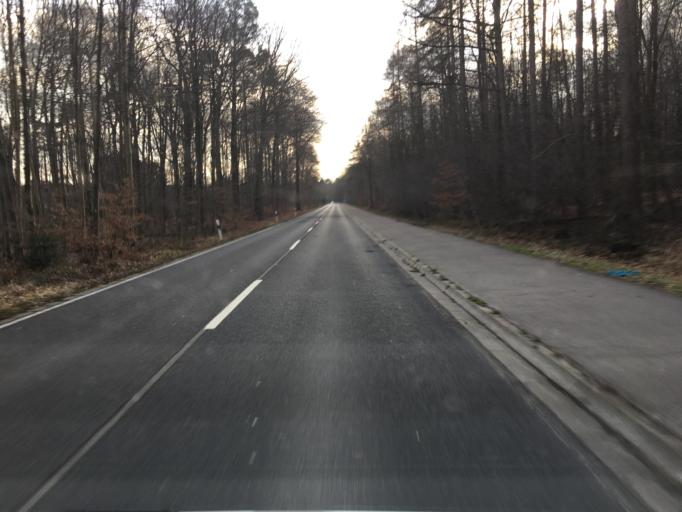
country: DE
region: North Rhine-Westphalia
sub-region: Regierungsbezirk Koln
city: Rosrath
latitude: 50.9187
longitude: 7.1539
